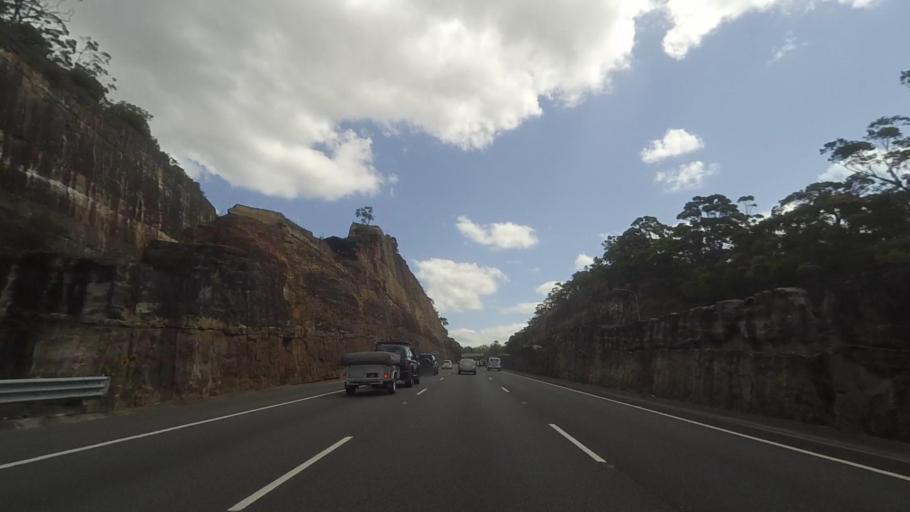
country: AU
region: New South Wales
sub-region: Hornsby Shire
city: Berowra
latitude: -33.6025
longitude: 151.1675
